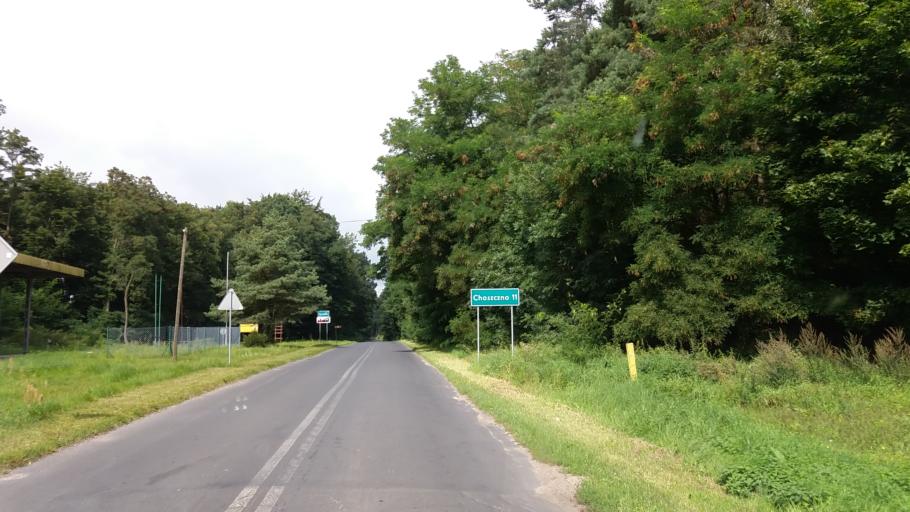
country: PL
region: West Pomeranian Voivodeship
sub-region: Powiat choszczenski
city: Krzecin
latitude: 53.0846
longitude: 15.4803
